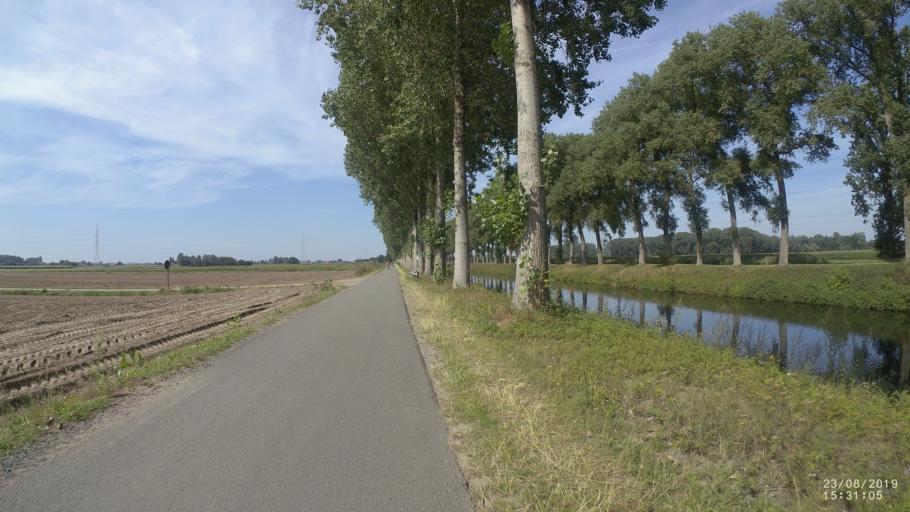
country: BE
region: Flanders
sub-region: Provincie Oost-Vlaanderen
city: Zomergem
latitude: 51.1512
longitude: 3.5516
